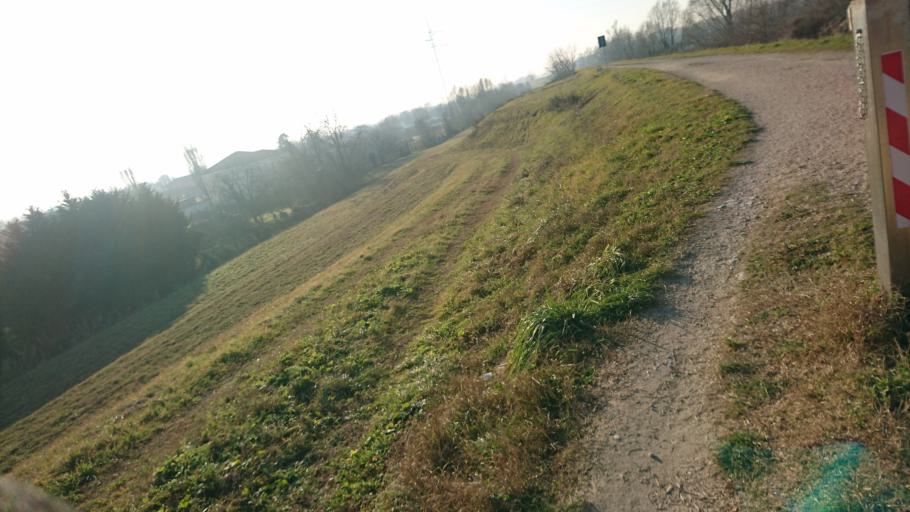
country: IT
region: Veneto
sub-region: Provincia di Rovigo
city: San Martino di Venezze
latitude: 45.1325
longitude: 11.8658
